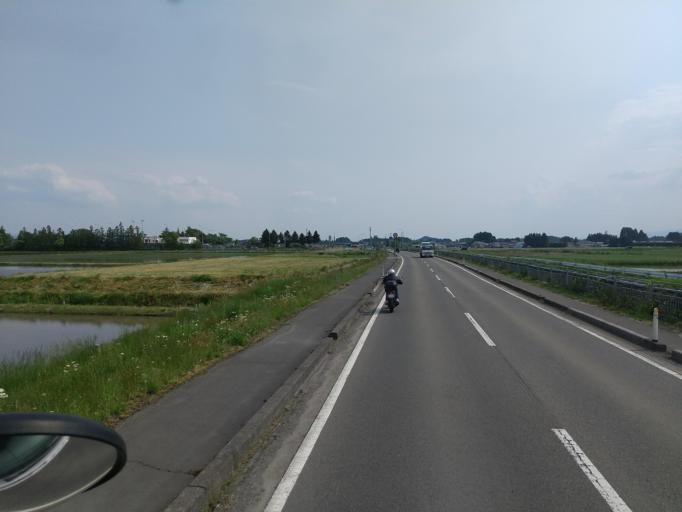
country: JP
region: Iwate
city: Hanamaki
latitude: 39.3883
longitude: 141.0873
